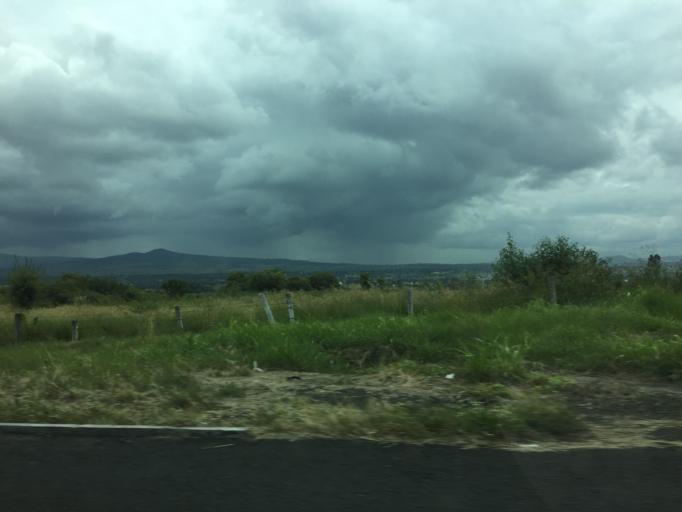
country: MX
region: Jalisco
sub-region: Zapotlanejo
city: La Mezquitera
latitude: 20.5921
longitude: -103.1067
